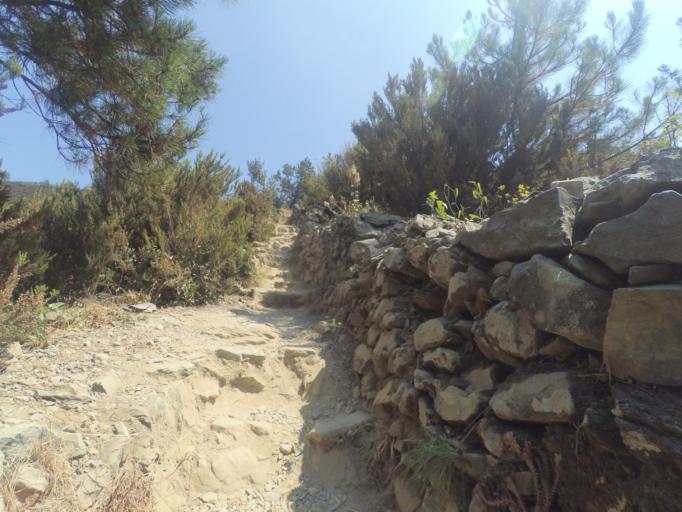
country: IT
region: Liguria
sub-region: Provincia di La Spezia
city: Riomaggiore
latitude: 44.1061
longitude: 9.7305
